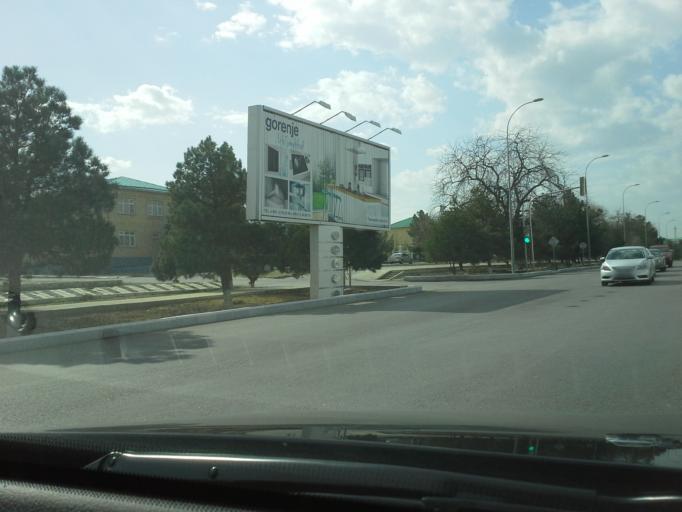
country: TM
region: Ahal
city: Ashgabat
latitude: 37.9575
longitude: 58.3231
